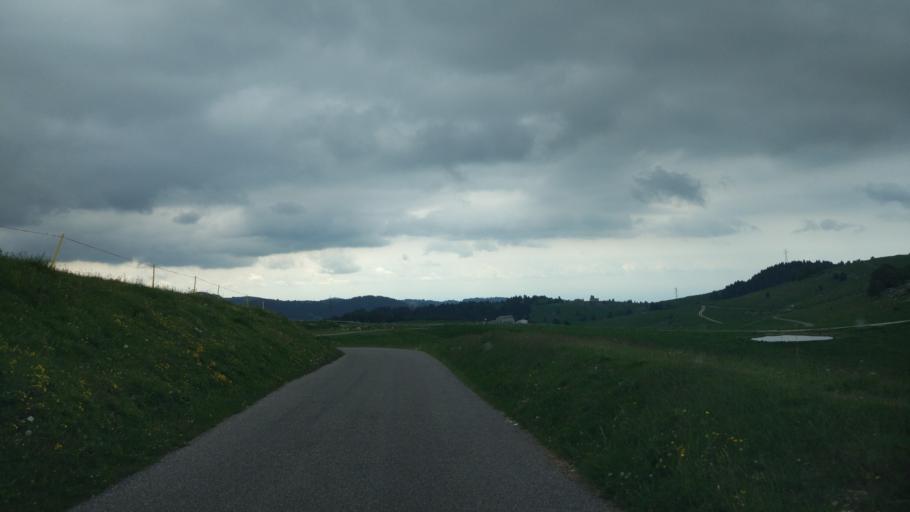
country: IT
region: Veneto
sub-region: Provincia di Verona
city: Erbezzo
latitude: 45.6895
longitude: 11.0032
